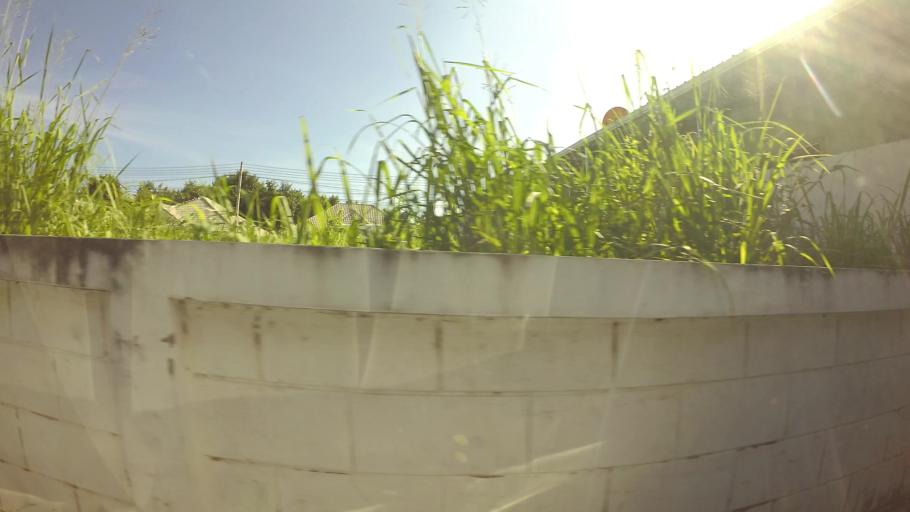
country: TH
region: Rayong
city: Rayong
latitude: 12.6673
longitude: 101.2979
